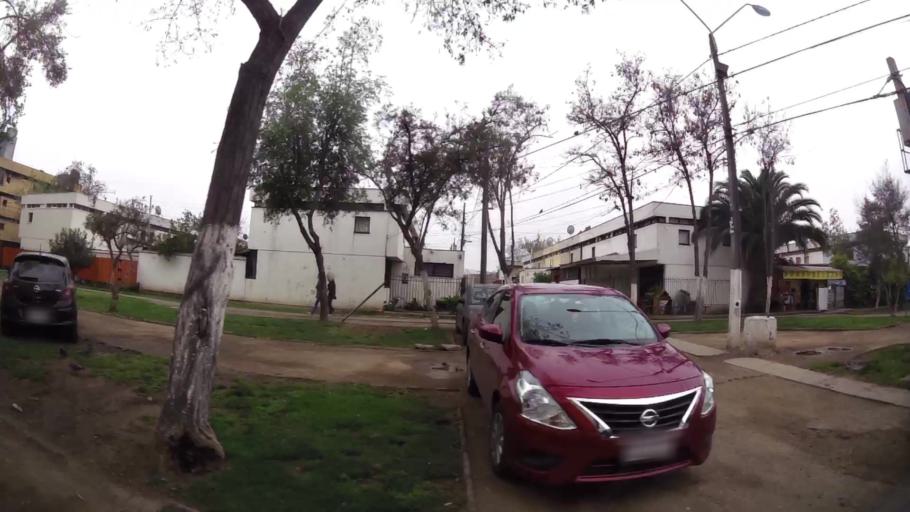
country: CL
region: Santiago Metropolitan
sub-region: Provincia de Santiago
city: Santiago
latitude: -33.4783
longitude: -70.6411
